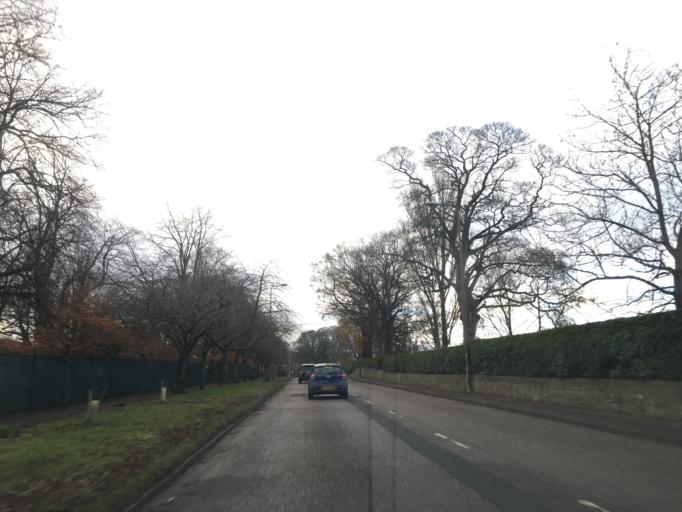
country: GB
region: Scotland
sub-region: Edinburgh
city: Colinton
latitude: 55.9127
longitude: -3.2454
